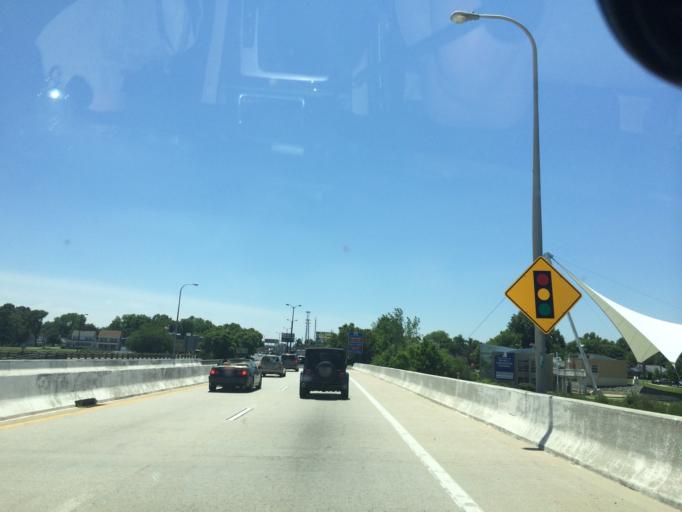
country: US
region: Maryland
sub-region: Dorchester County
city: Cambridge
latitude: 38.5723
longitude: -76.0627
